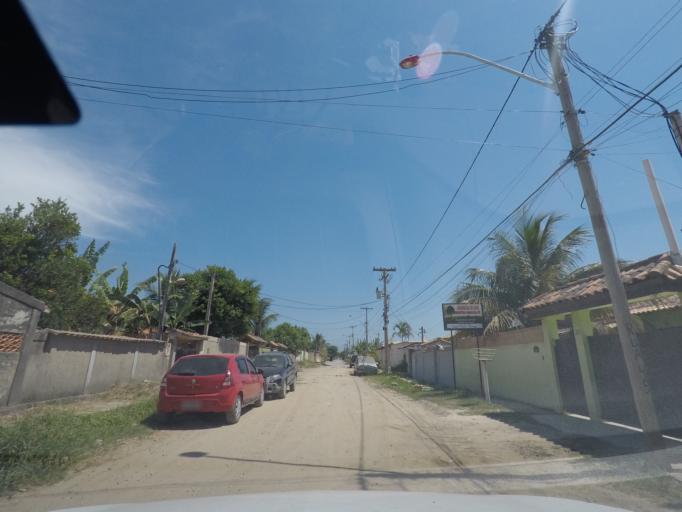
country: BR
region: Rio de Janeiro
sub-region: Marica
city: Marica
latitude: -22.9548
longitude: -42.9568
